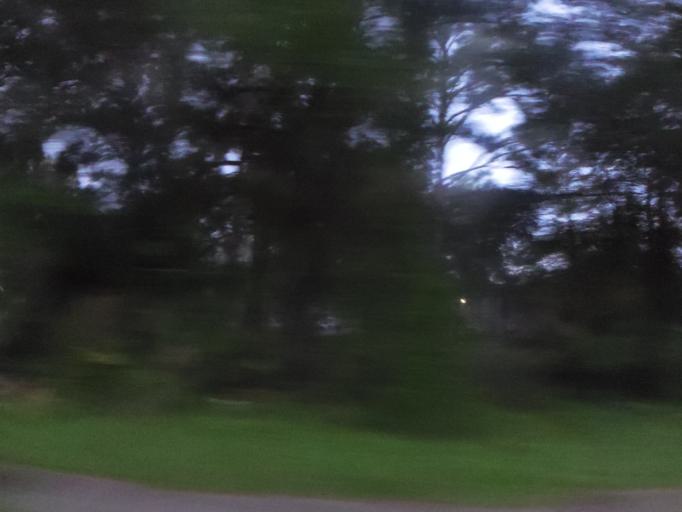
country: US
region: Florida
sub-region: Duval County
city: Jacksonville
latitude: 30.2440
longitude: -81.6138
